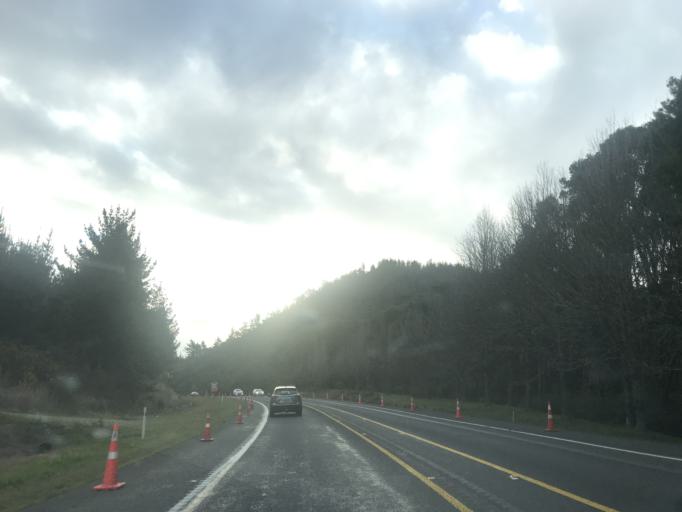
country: NZ
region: Bay of Plenty
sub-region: Western Bay of Plenty District
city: Waihi Beach
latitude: -37.4558
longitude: 175.9005
